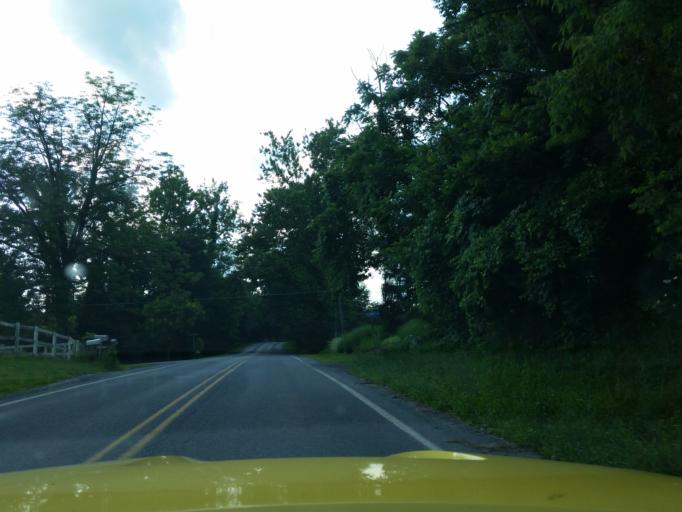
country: US
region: Pennsylvania
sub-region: Lebanon County
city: Jonestown
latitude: 40.4189
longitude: -76.5366
